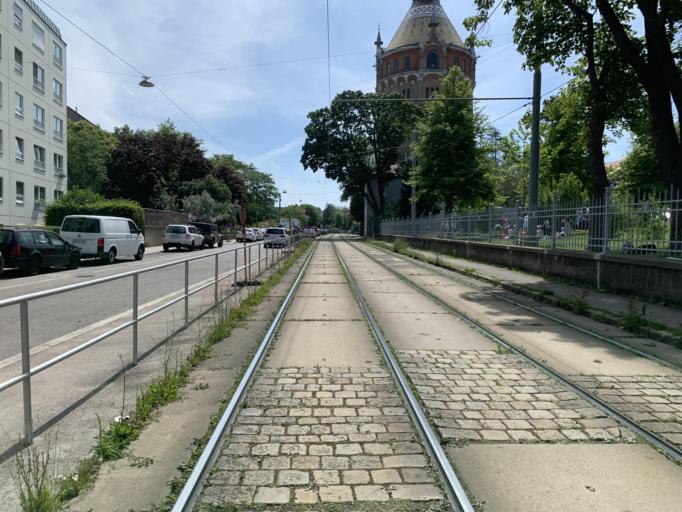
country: AT
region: Vienna
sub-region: Wien Stadt
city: Vienna
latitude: 48.1699
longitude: 16.3525
